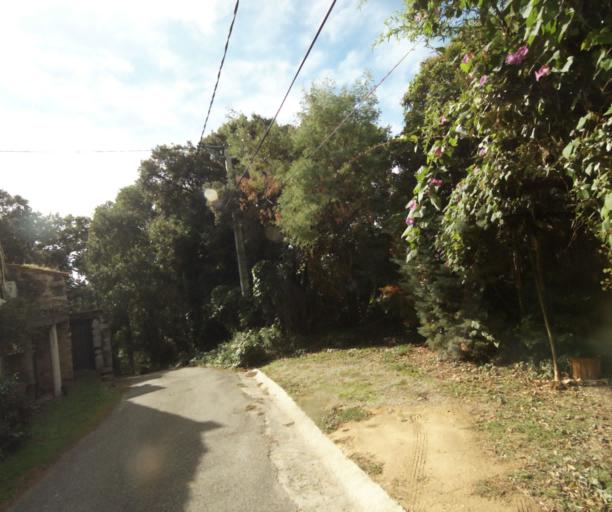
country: FR
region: Languedoc-Roussillon
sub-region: Departement des Pyrenees-Orientales
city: Sant Andreu de Sureda
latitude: 42.5311
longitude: 2.9898
